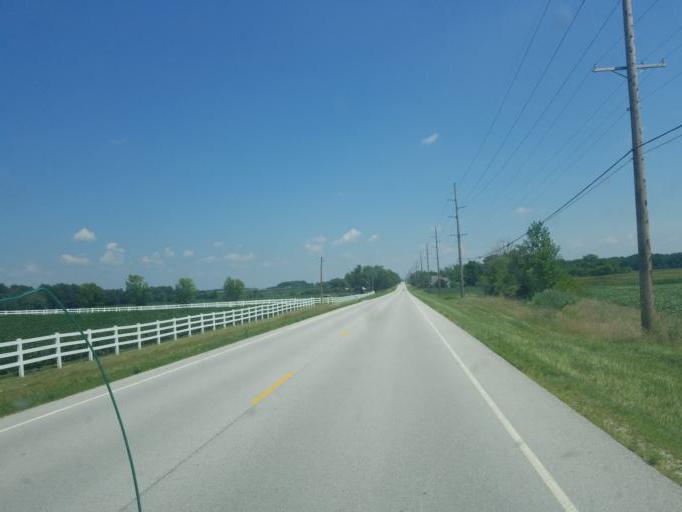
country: US
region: Ohio
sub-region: Auglaize County
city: Saint Marys
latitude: 40.5540
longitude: -84.3140
